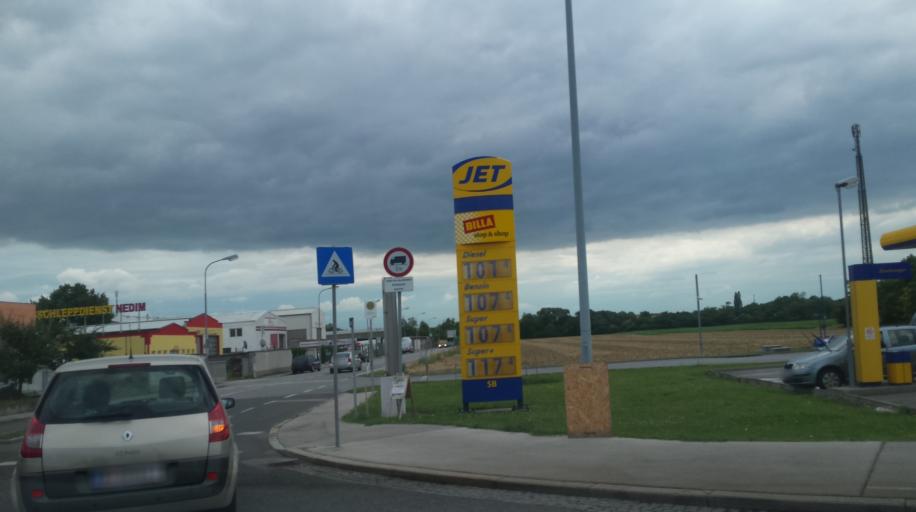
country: AT
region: Lower Austria
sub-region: Politischer Bezirk Wien-Umgebung
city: Lanzendorf
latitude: 48.1175
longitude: 16.4533
